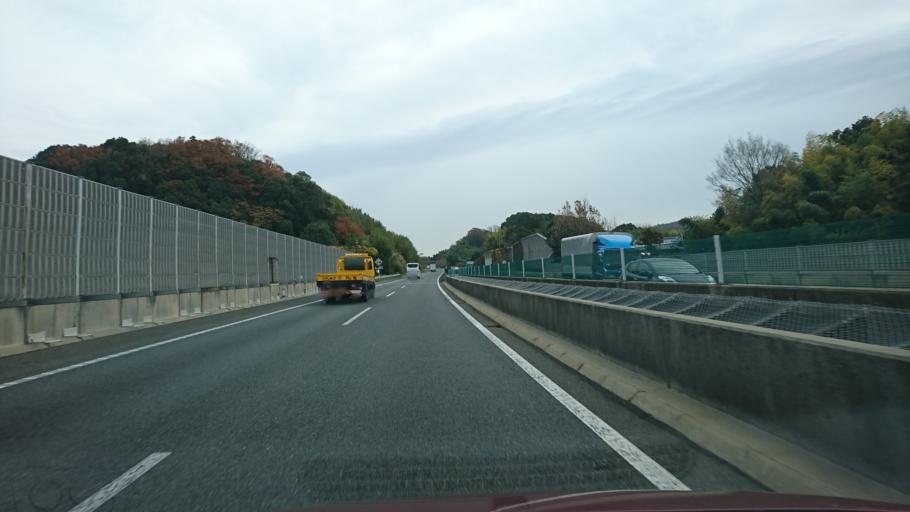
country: JP
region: Hyogo
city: Sandacho
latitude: 34.8219
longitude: 135.1299
